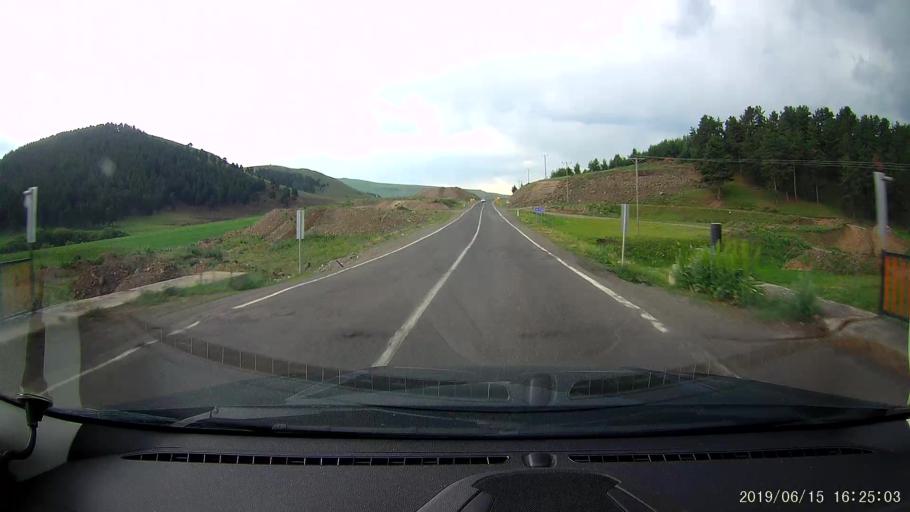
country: TR
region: Ardahan
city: Hanak
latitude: 41.1589
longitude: 42.8717
